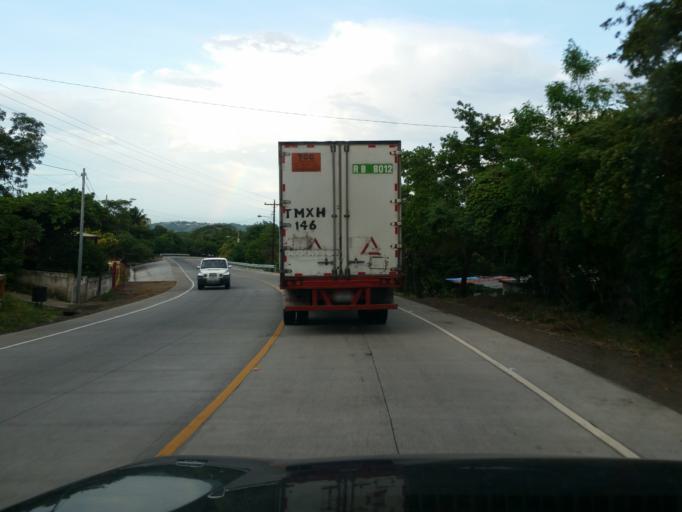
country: NI
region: Managua
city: Ciudad Sandino
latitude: 12.0804
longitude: -86.3654
